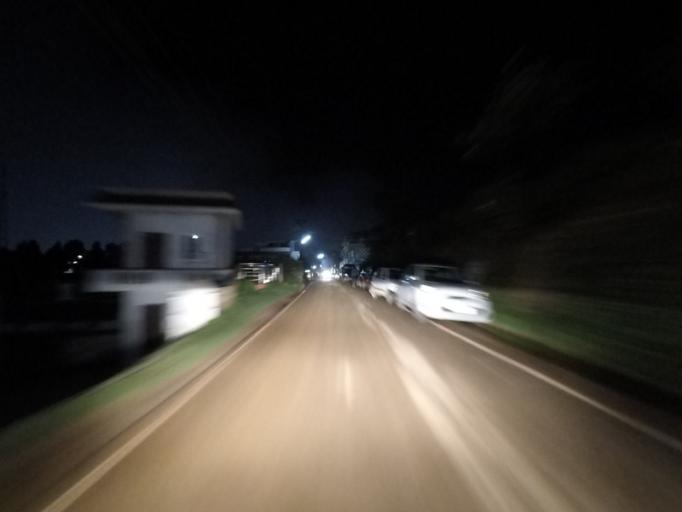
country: IN
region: Tamil Nadu
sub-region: Nilgiri
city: Kotagiri
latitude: 11.4276
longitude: 76.8670
